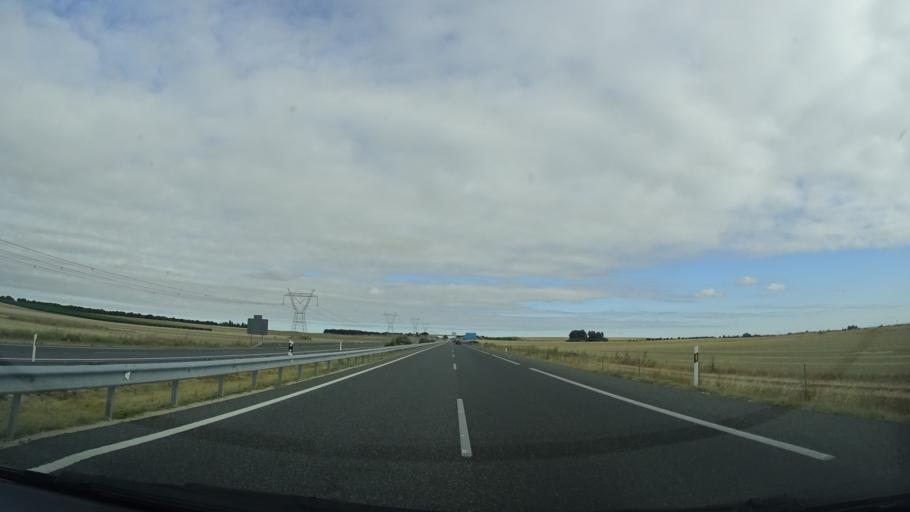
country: ES
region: Castille and Leon
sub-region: Provincia de Valladolid
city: San Pablo de la Moraleja
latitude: 41.1406
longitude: -4.7822
